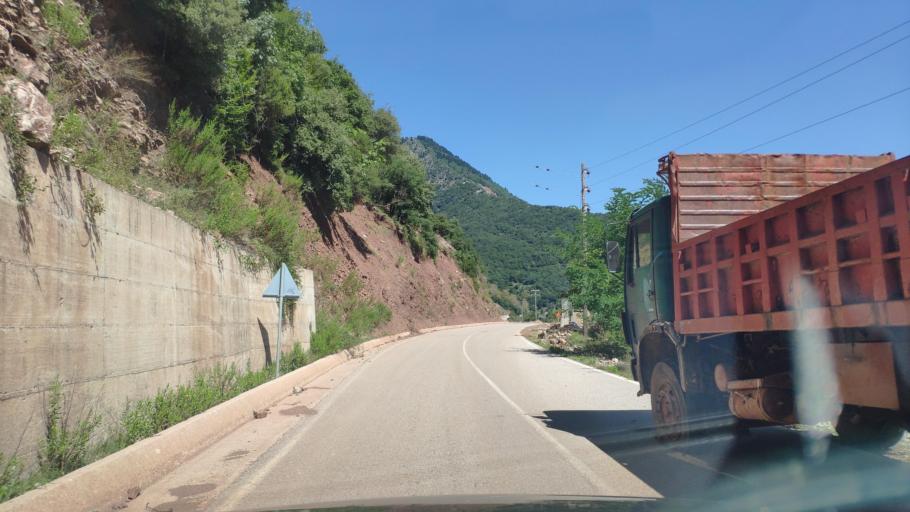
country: GR
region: Central Greece
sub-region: Nomos Evrytanias
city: Kerasochori
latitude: 39.0808
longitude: 21.5965
